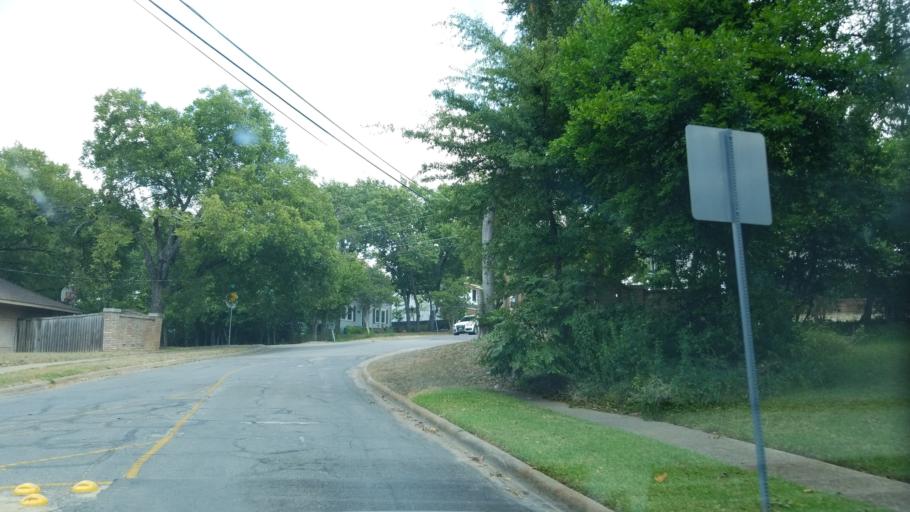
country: US
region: Texas
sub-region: Dallas County
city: Cockrell Hill
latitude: 32.7546
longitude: -96.8485
